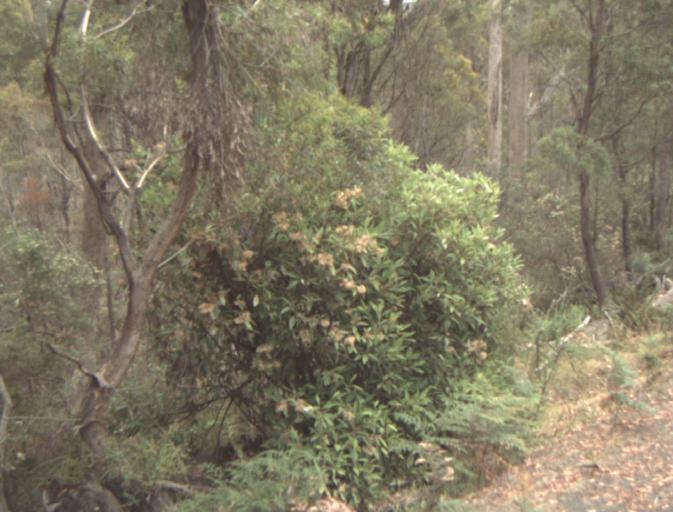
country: AU
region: Tasmania
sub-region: Northern Midlands
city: Evandale
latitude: -41.4837
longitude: 147.5385
